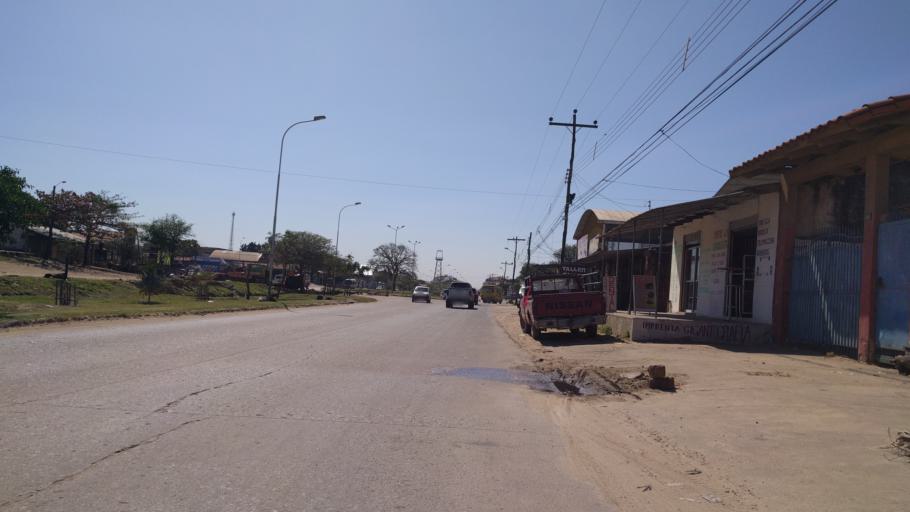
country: BO
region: Santa Cruz
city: Santa Cruz de la Sierra
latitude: -17.8184
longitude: -63.2267
